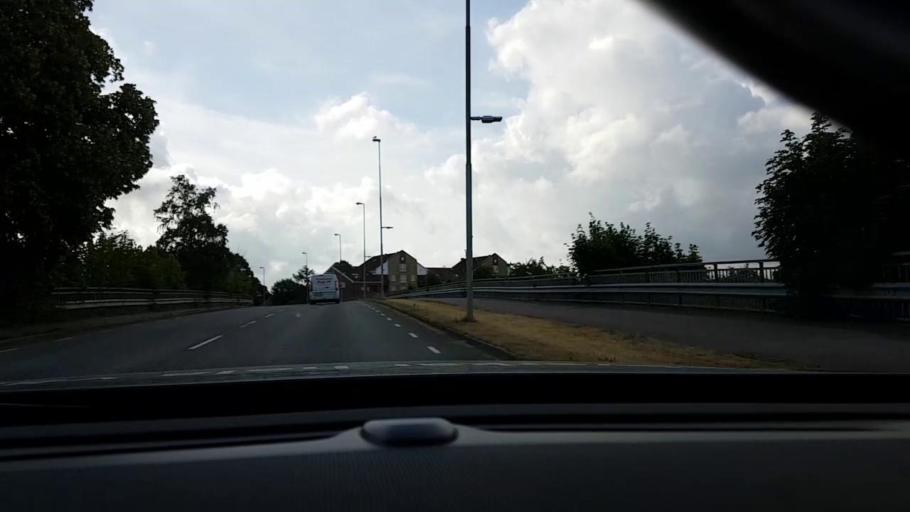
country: SE
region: Skane
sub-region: Hassleholms Kommun
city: Hassleholm
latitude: 56.1612
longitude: 13.7636
